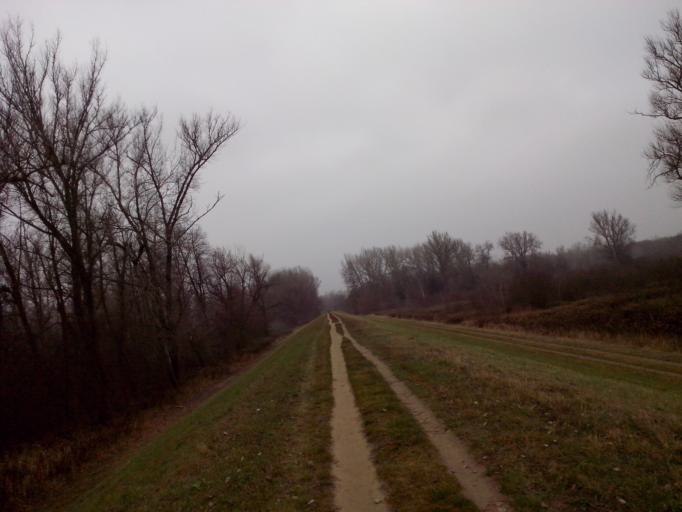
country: PL
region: Masovian Voivodeship
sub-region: Powiat legionowski
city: Jablonna
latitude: 52.3571
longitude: 20.9201
